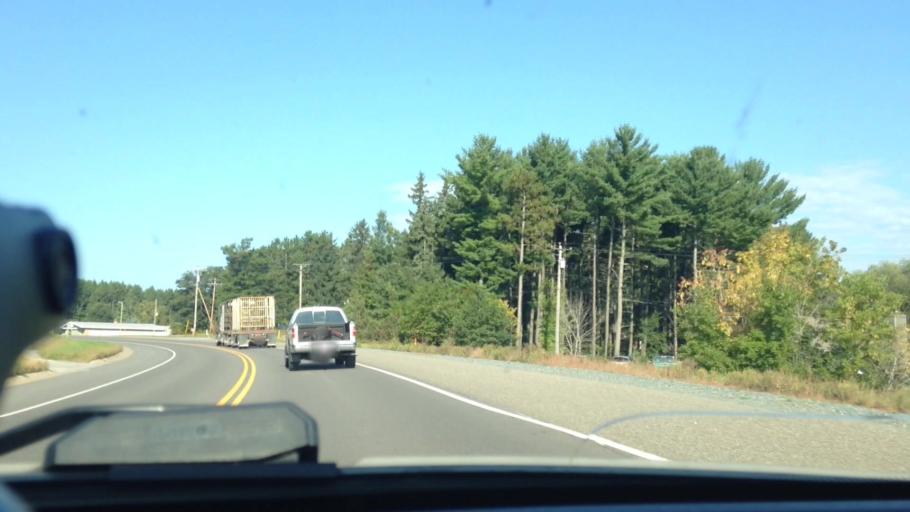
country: US
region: Michigan
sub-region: Dickinson County
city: Iron Mountain
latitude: 45.8756
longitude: -88.0871
